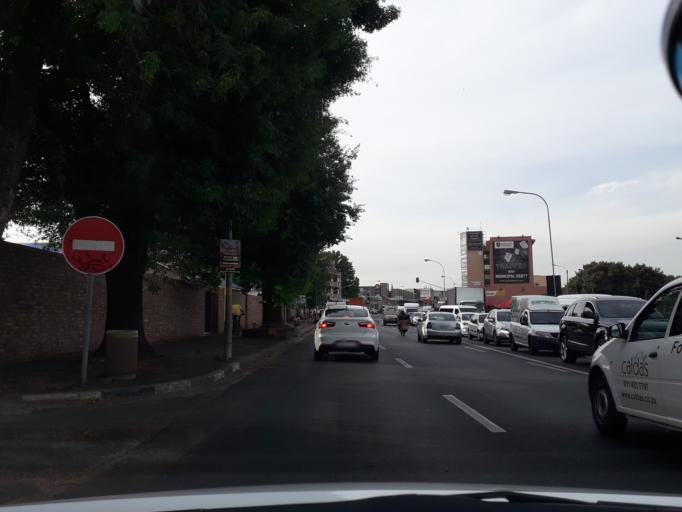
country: ZA
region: Gauteng
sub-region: City of Johannesburg Metropolitan Municipality
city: Modderfontein
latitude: -26.1510
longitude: 28.1587
